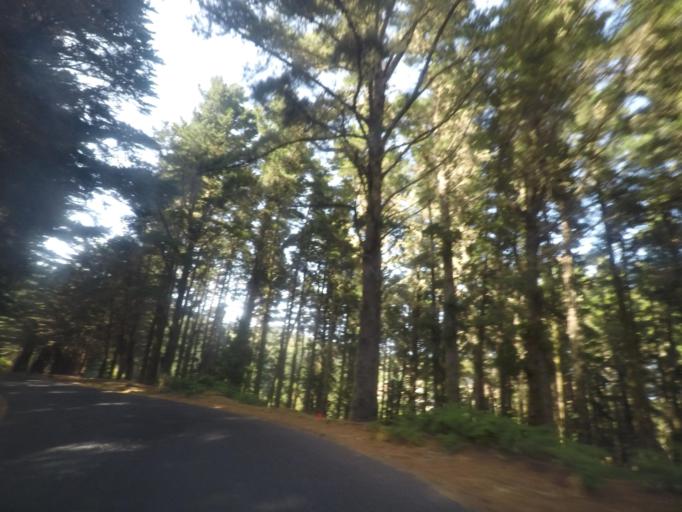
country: PT
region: Madeira
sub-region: Santa Cruz
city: Camacha
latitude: 32.7040
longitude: -16.8791
